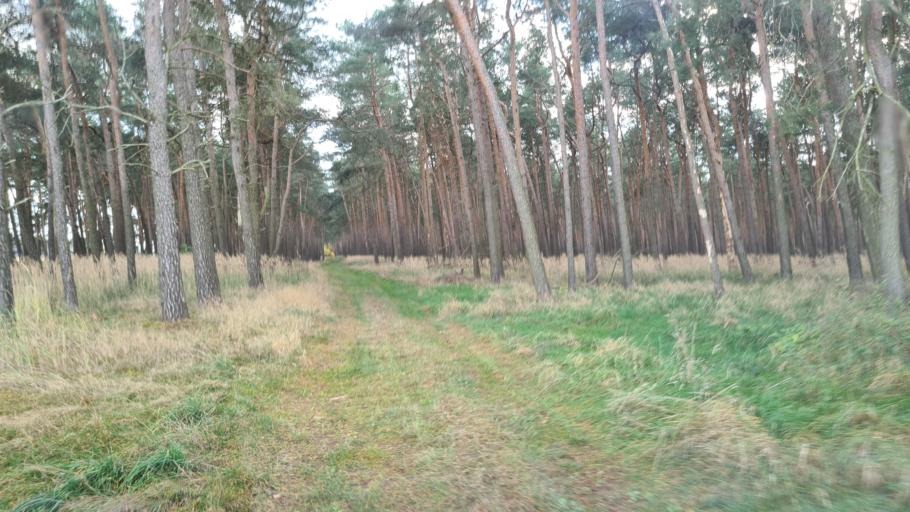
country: DE
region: Saxony-Anhalt
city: Zahna
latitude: 51.9721
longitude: 12.8136
